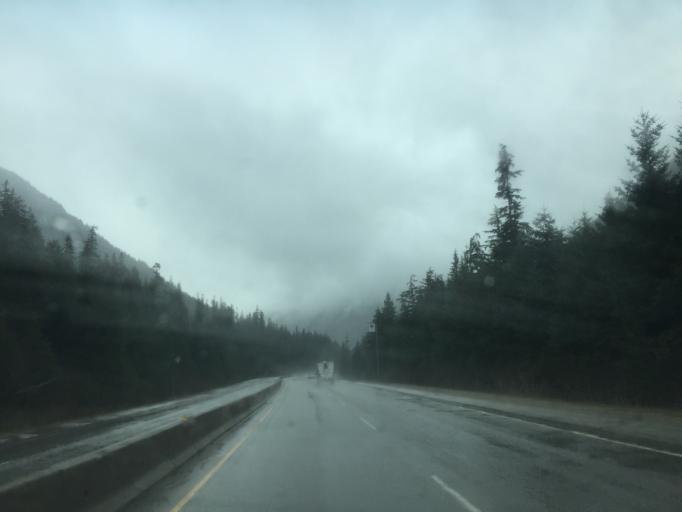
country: CA
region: British Columbia
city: Hope
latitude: 49.5464
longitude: -121.1953
